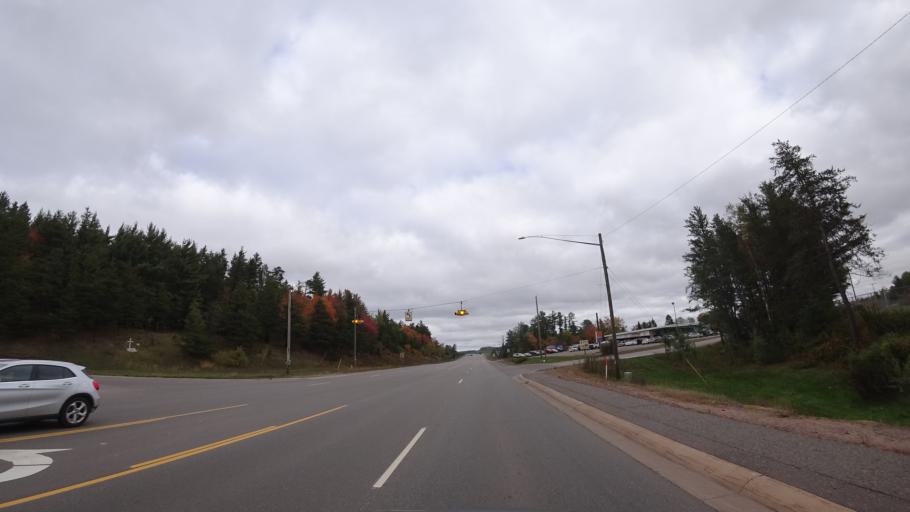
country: US
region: Michigan
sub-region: Marquette County
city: West Ishpeming
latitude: 46.4886
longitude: -87.7110
